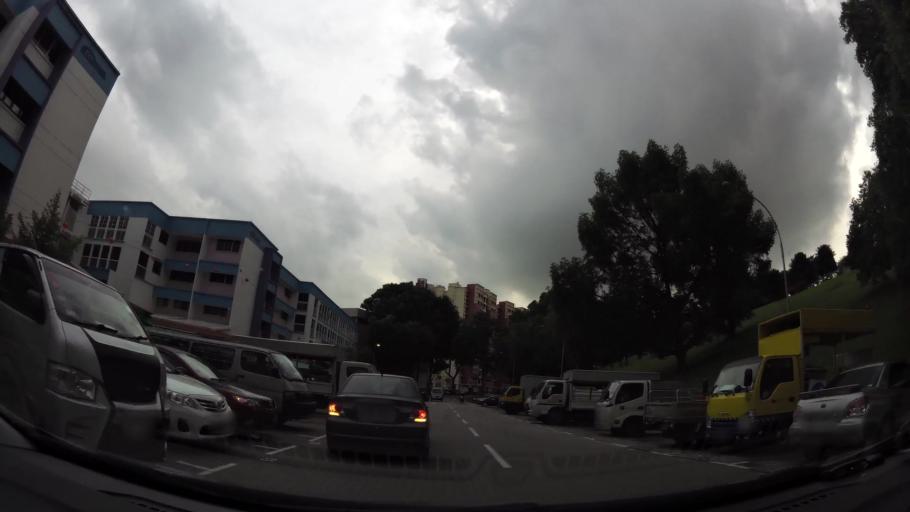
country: MY
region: Johor
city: Kampung Pasir Gudang Baru
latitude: 1.4370
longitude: 103.8367
